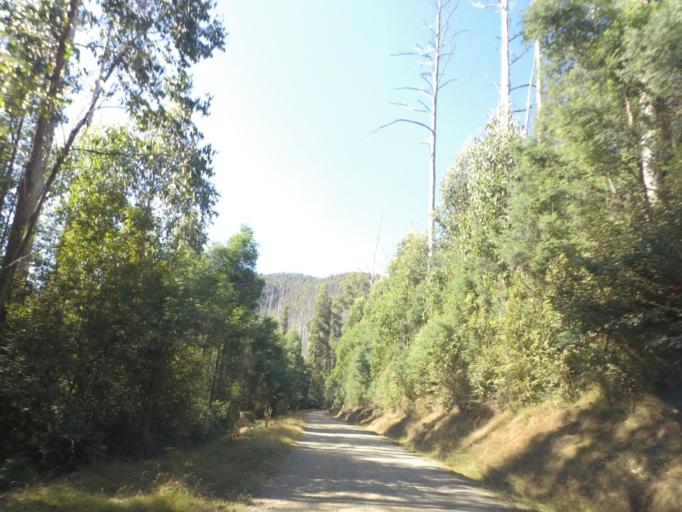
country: AU
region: Victoria
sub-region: Yarra Ranges
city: Millgrove
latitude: -37.5014
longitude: 145.8058
